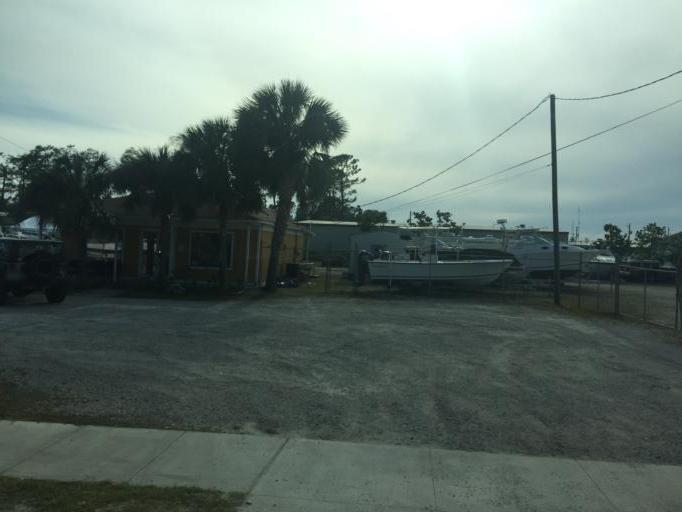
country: US
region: Florida
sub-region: Bay County
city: Upper Grand Lagoon
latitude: 30.1808
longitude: -85.7608
